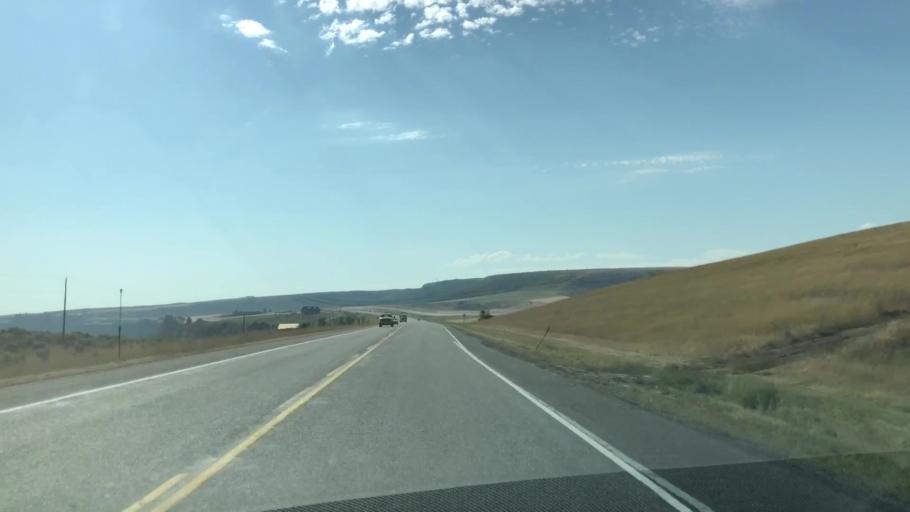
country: US
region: Idaho
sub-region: Madison County
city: Rexburg
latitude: 43.6005
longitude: -111.6502
